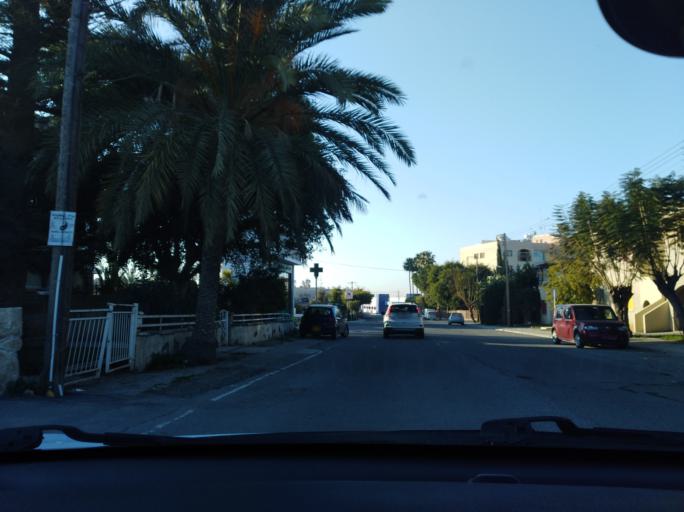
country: CY
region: Limassol
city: Mouttagiaka
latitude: 34.7051
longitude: 33.1065
